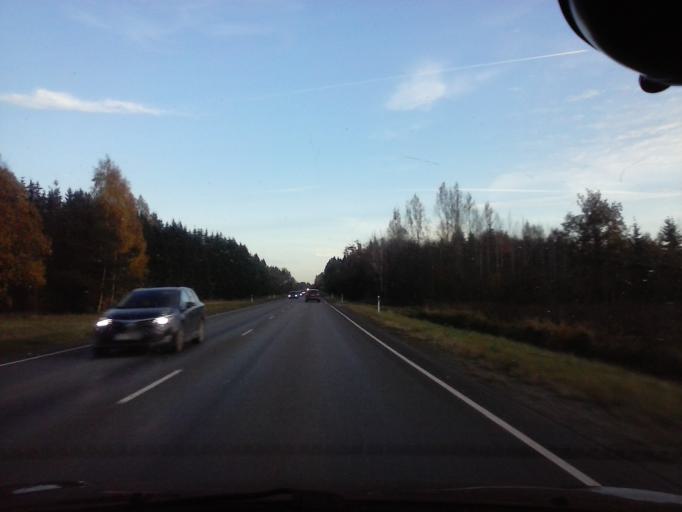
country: EE
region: Harju
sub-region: Nissi vald
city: Turba
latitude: 58.9381
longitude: 24.0917
